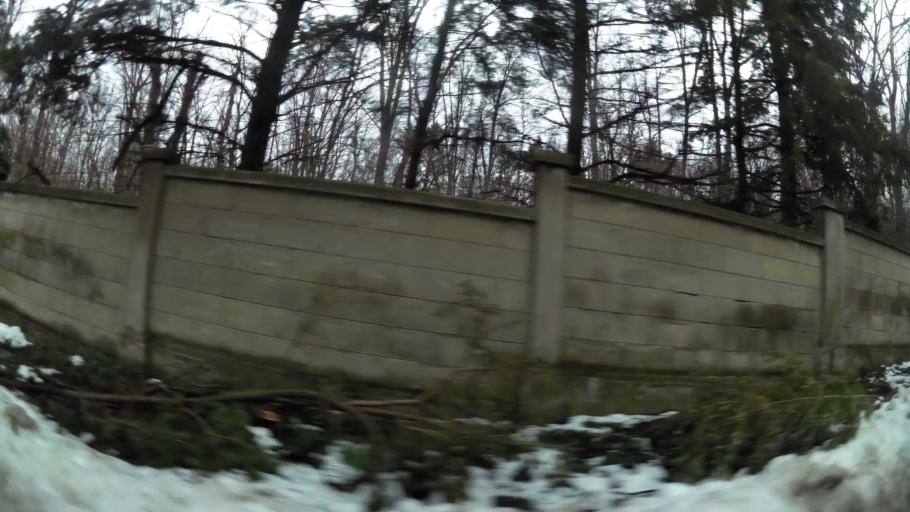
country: RS
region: Central Serbia
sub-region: Belgrade
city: Savski Venac
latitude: 44.7626
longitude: 20.4537
